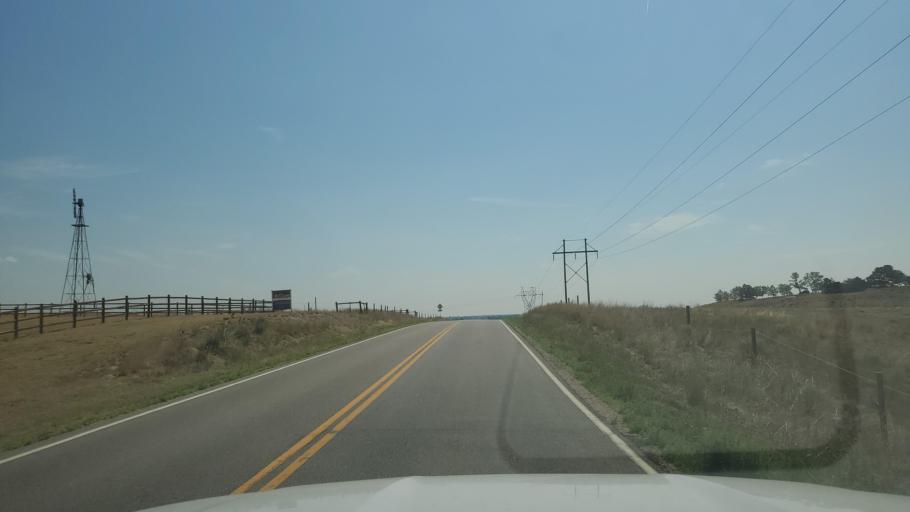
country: US
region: Colorado
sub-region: Adams County
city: Todd Creek
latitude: 39.9431
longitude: -104.8792
